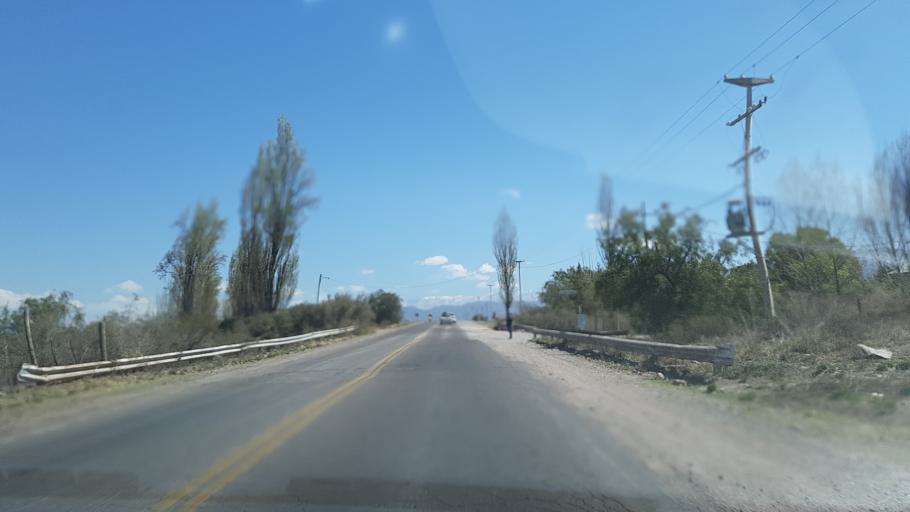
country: AR
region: Mendoza
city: Lujan de Cuyo
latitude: -33.0173
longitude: -68.9372
